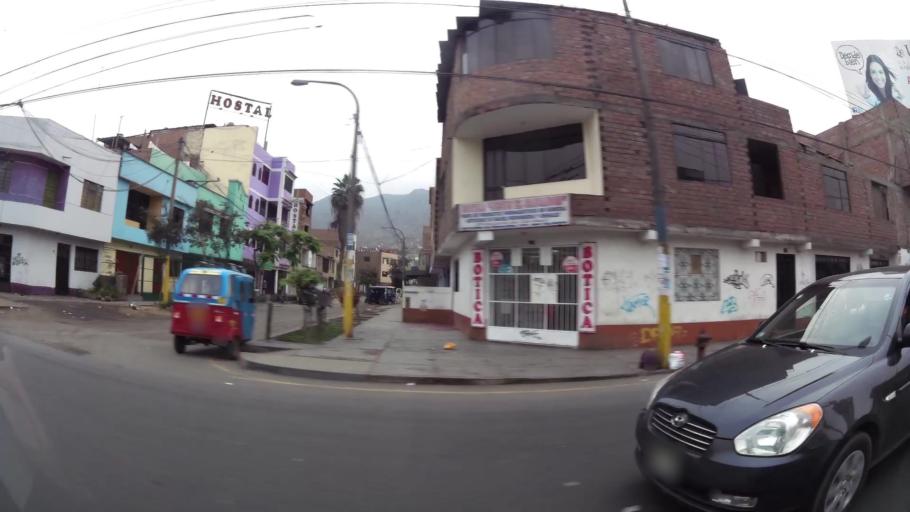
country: PE
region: Lima
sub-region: Lima
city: Independencia
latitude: -11.9978
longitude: -77.0150
